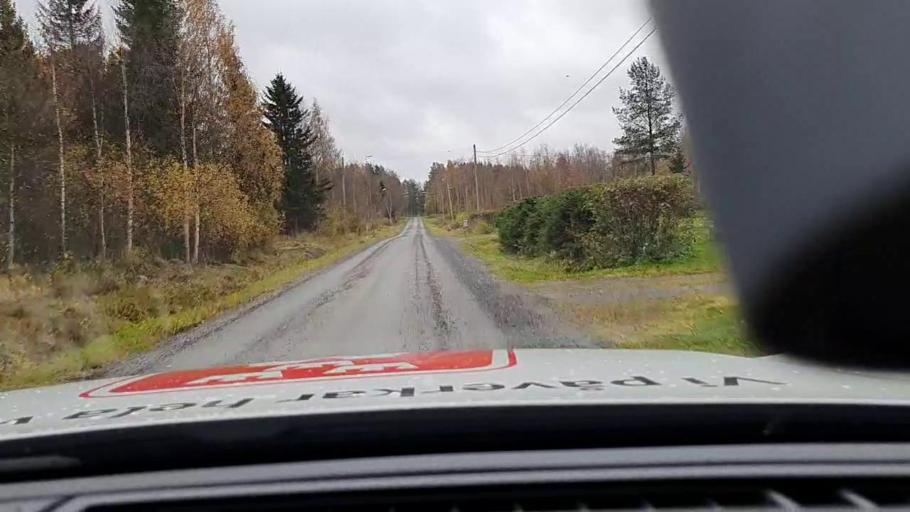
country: FI
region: Lapland
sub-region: Kemi-Tornio
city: Tornio
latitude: 65.9764
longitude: 24.0219
